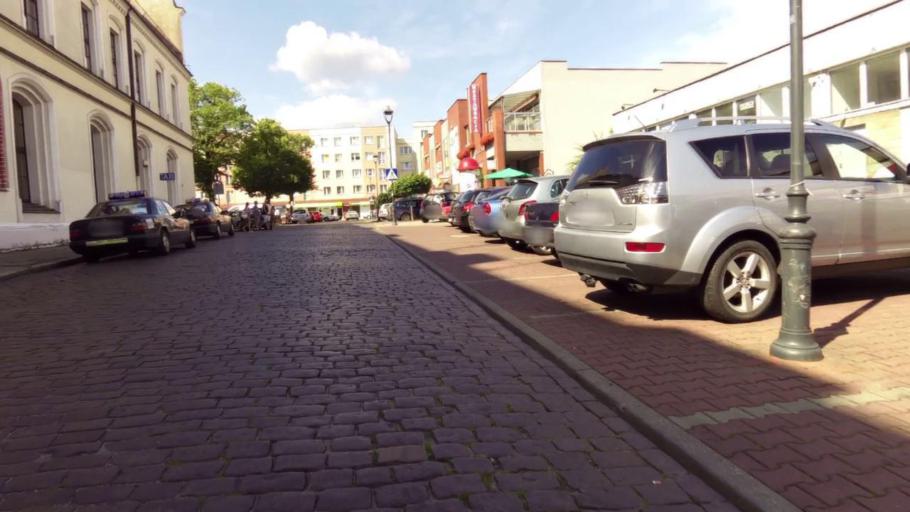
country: PL
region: West Pomeranian Voivodeship
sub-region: Powiat stargardzki
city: Stargard Szczecinski
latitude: 53.3375
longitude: 15.0464
